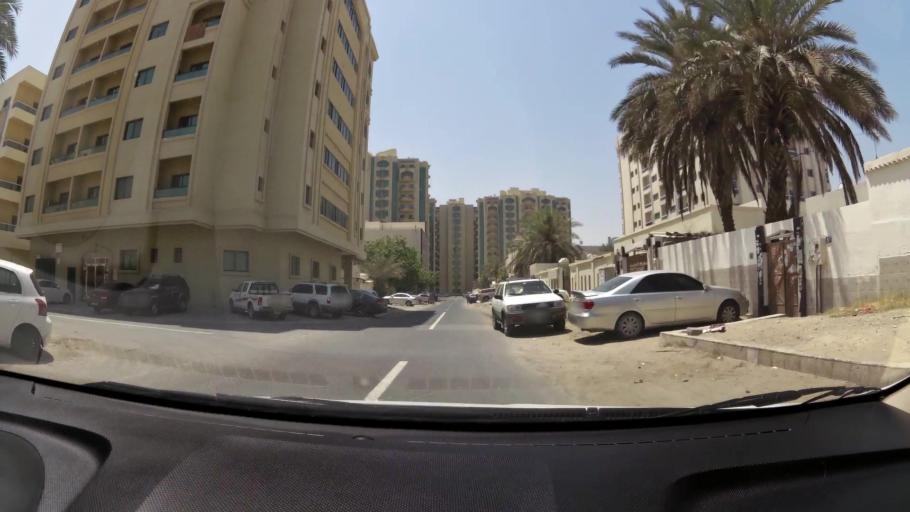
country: AE
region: Ajman
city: Ajman
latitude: 25.3965
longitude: 55.4498
